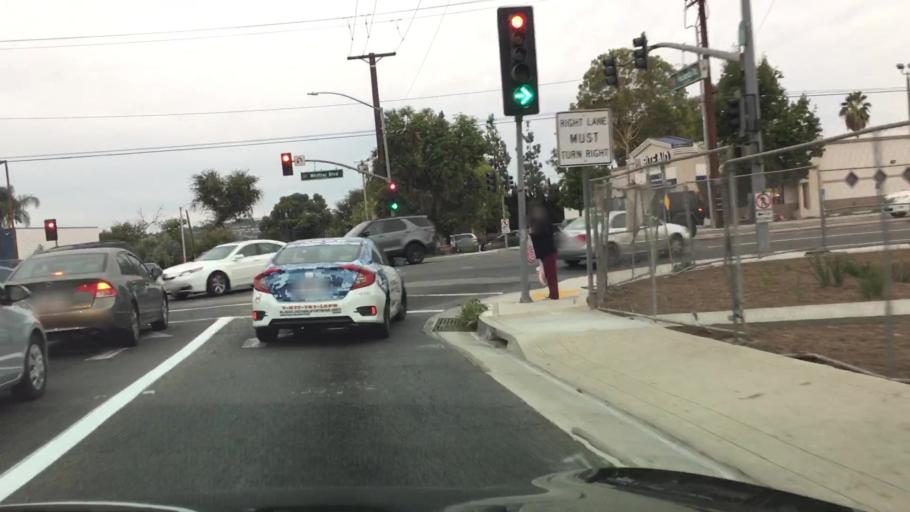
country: US
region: California
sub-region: Orange County
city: La Habra
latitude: 33.9399
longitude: -117.9648
